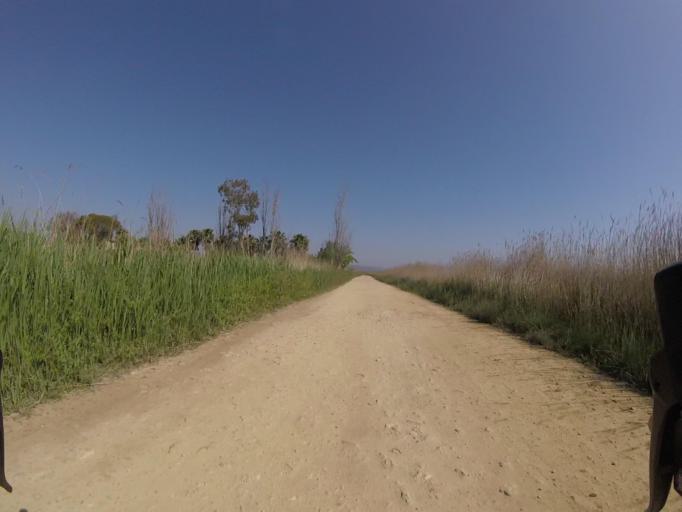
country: ES
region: Valencia
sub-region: Provincia de Castello
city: Torreblanca
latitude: 40.1620
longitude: 0.1721
